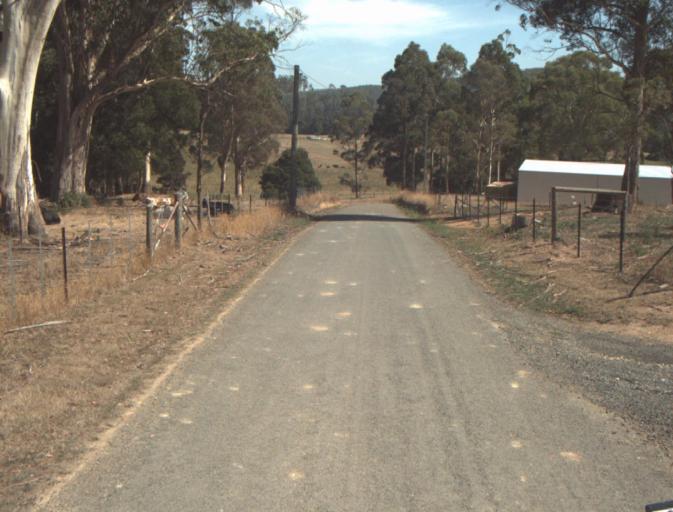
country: AU
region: Tasmania
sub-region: Launceston
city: Mayfield
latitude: -41.2338
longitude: 147.2551
